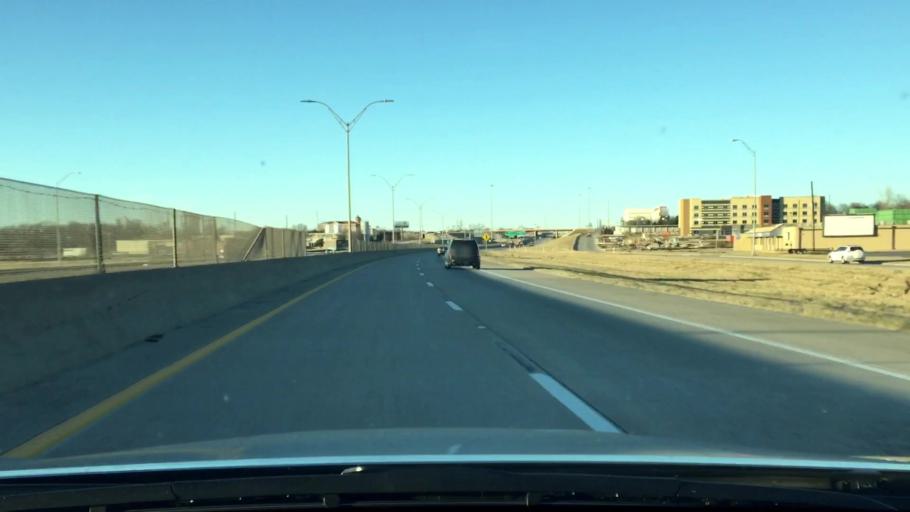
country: US
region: Texas
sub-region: Cooke County
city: Gainesville
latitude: 33.6327
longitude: -97.1553
